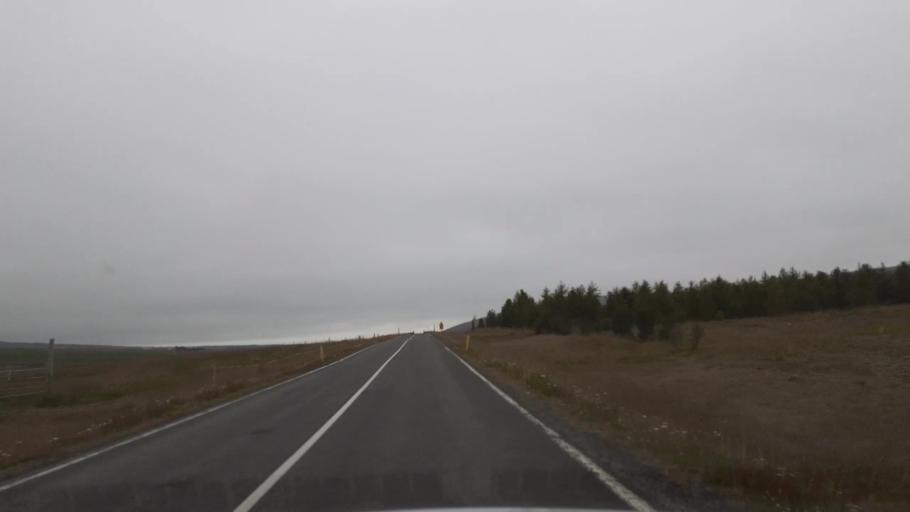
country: IS
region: Northeast
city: Siglufjoerdur
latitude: 65.7382
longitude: -19.1328
